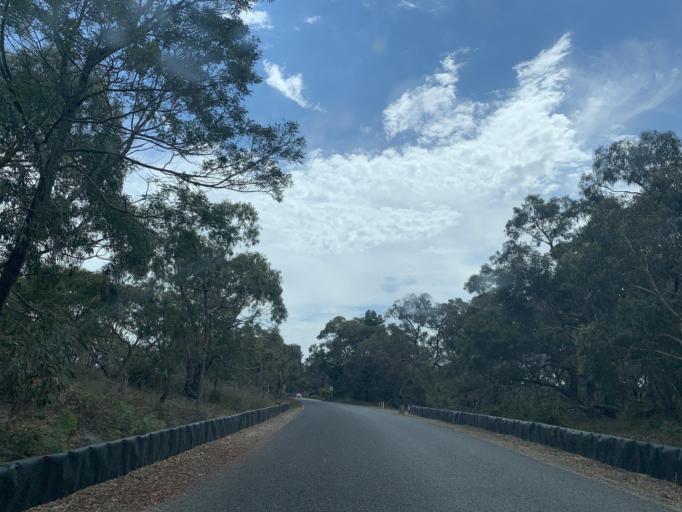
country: AU
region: Victoria
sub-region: Casey
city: Botanic Ridge
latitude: -38.1267
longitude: 145.2725
